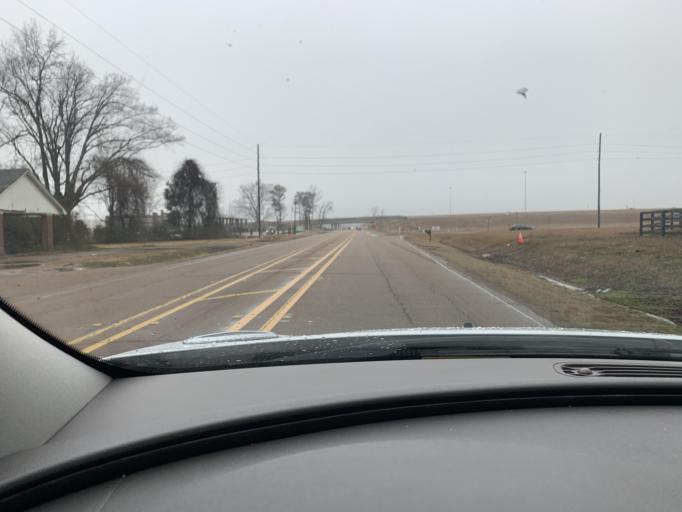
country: US
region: Mississippi
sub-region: De Soto County
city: Hernando
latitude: 34.8579
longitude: -89.9952
